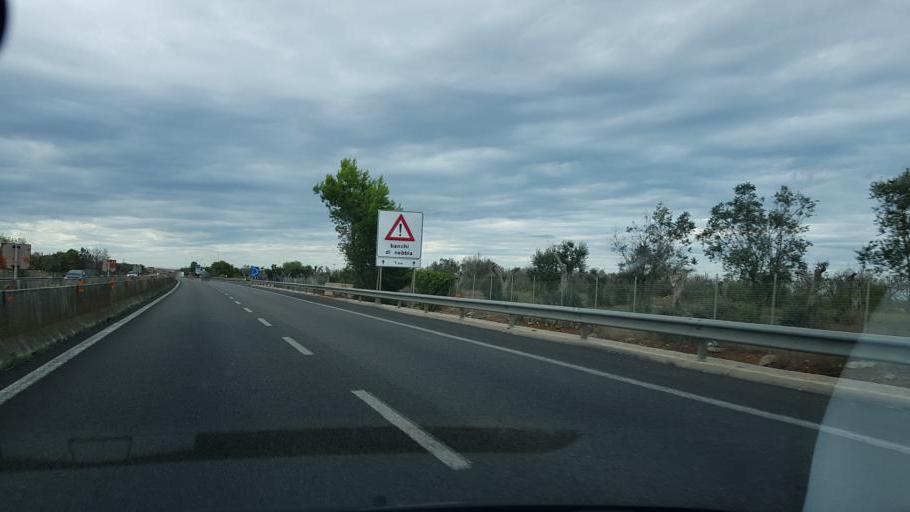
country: IT
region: Apulia
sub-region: Provincia di Lecce
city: Trepuzzi
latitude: 40.4171
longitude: 18.0993
